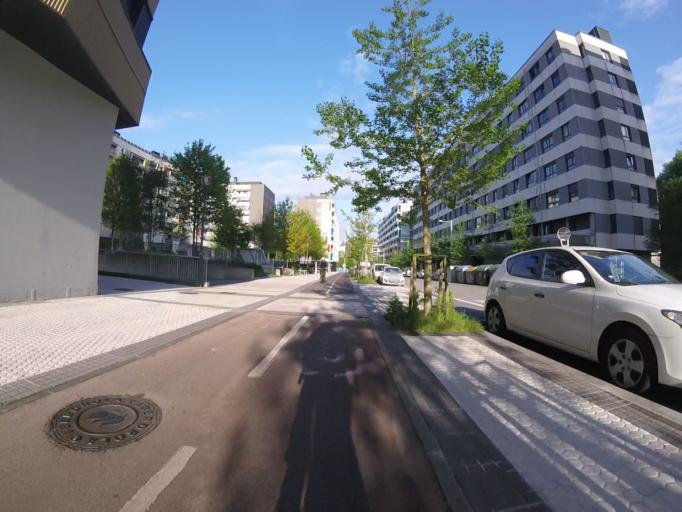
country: ES
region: Basque Country
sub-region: Provincia de Guipuzcoa
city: San Sebastian
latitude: 43.3084
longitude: -1.9852
